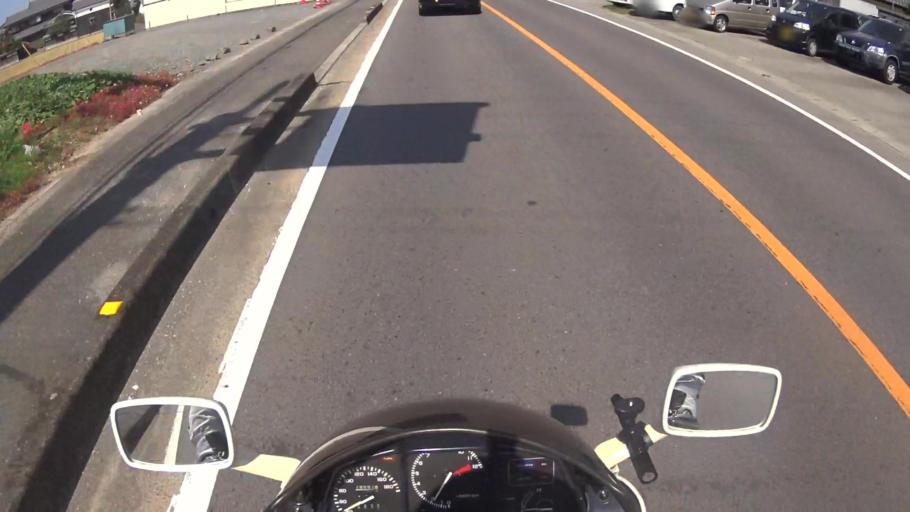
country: JP
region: Kyoto
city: Kameoka
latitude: 34.9985
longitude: 135.5518
